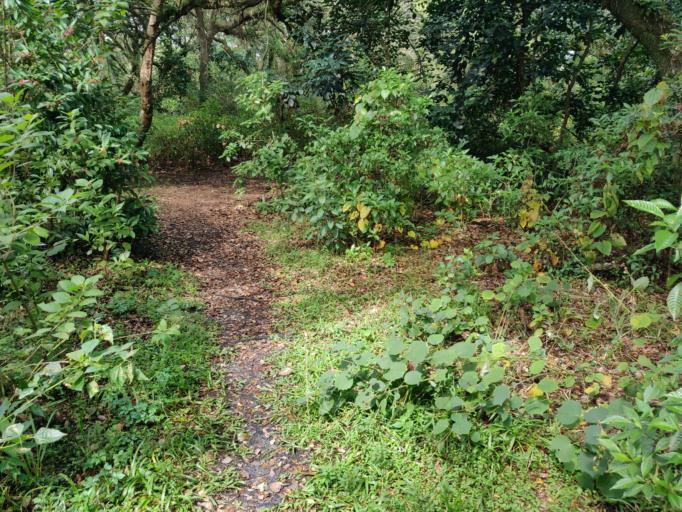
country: US
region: Florida
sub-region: Broward County
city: Cooper City
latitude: 26.0752
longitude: -80.2753
